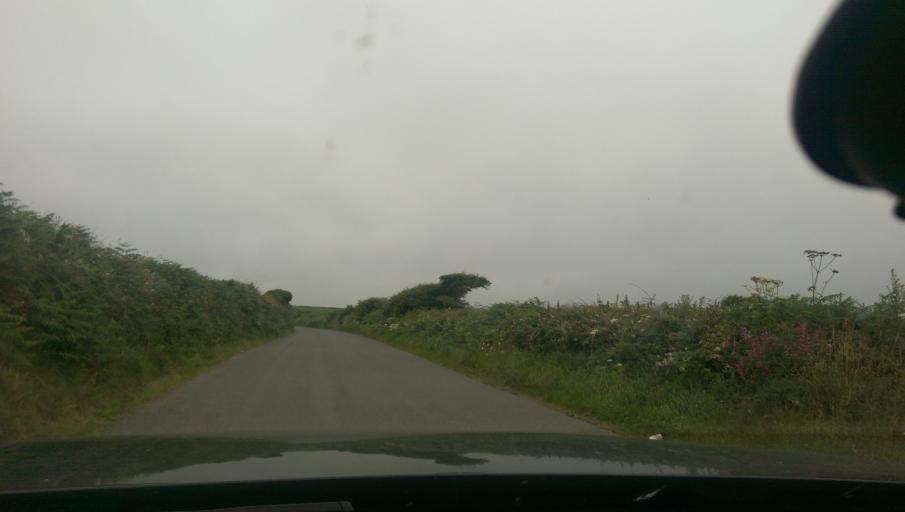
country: GB
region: England
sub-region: Cornwall
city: St. Buryan
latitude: 50.0937
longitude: -5.6456
